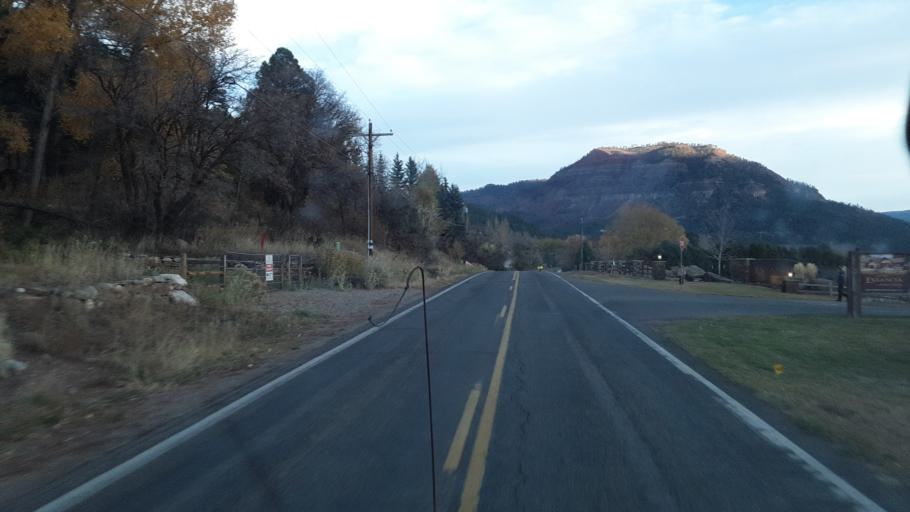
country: US
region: Colorado
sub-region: La Plata County
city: Durango
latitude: 37.4000
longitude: -107.8465
